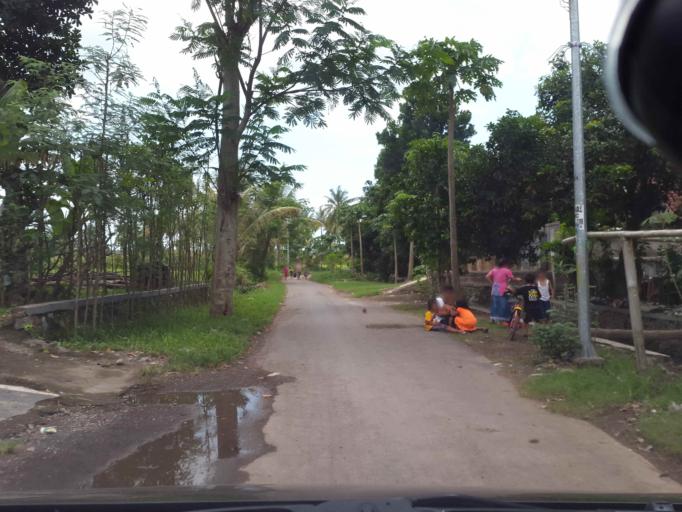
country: ID
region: West Nusa Tenggara
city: Kediri
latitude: -8.6405
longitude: 116.1393
